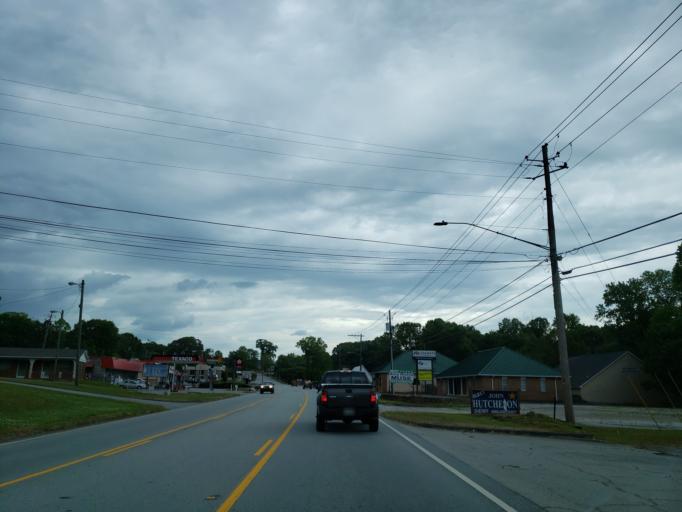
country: US
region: Georgia
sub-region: Haralson County
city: Bremen
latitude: 33.7141
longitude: -85.1420
